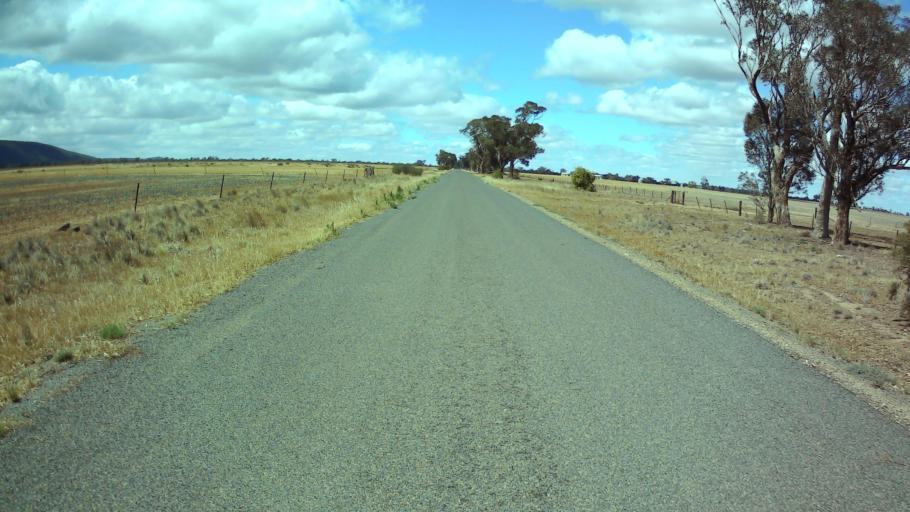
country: AU
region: New South Wales
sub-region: Weddin
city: Grenfell
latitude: -33.8731
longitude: 147.9262
